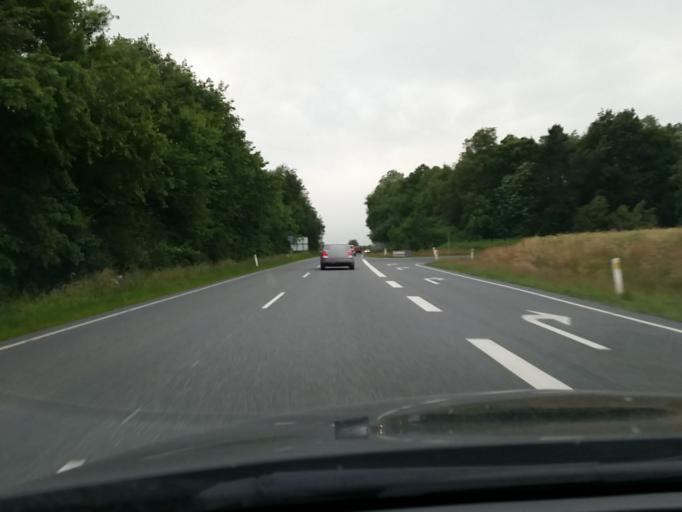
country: DK
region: South Denmark
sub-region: Varde Kommune
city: Olgod
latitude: 55.6540
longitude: 8.6788
